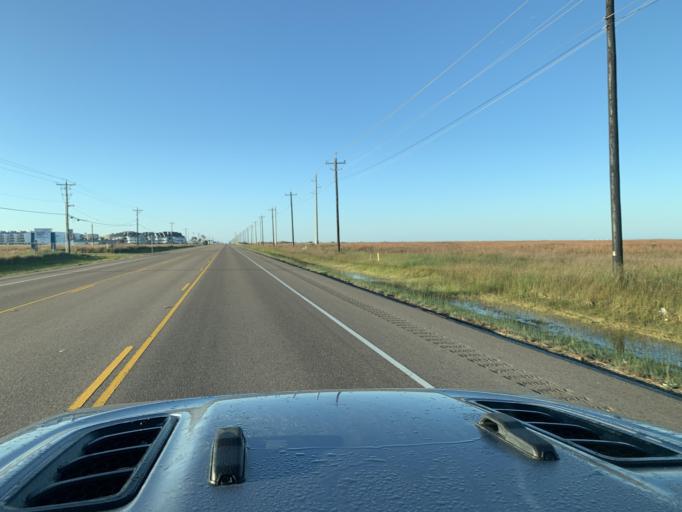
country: US
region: Texas
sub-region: Nueces County
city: Port Aransas
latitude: 27.7495
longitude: -97.1251
